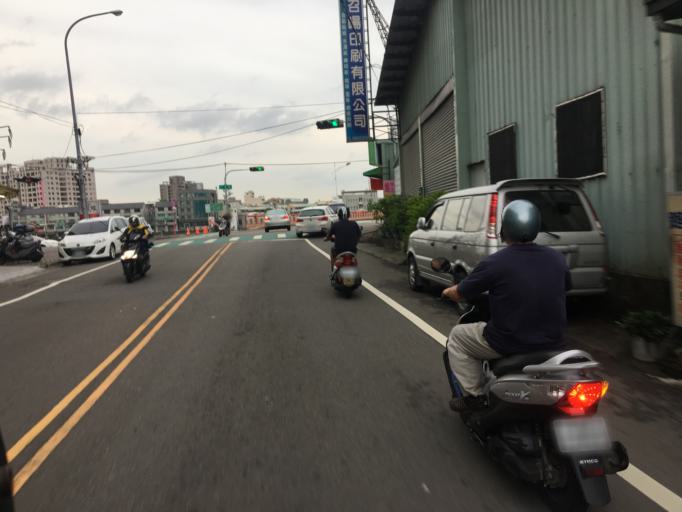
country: TW
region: Taiwan
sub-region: Taichung City
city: Taichung
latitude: 24.0999
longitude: 120.7015
